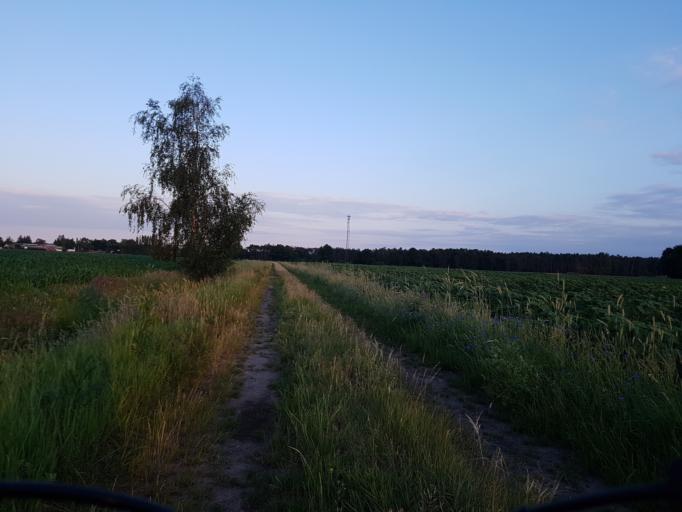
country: DE
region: Brandenburg
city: Schilda
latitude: 51.5808
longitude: 13.3511
